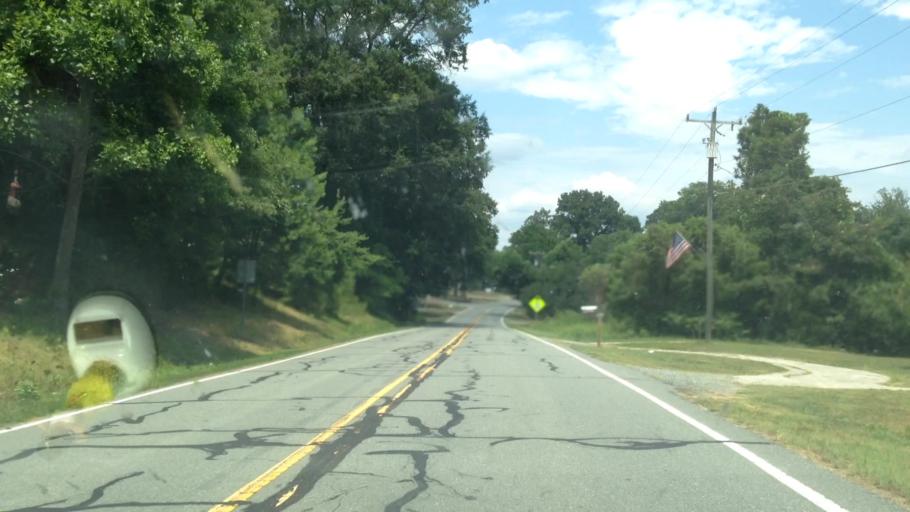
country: US
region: North Carolina
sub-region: Stokes County
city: Walnut Cove
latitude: 36.3228
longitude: -80.0498
